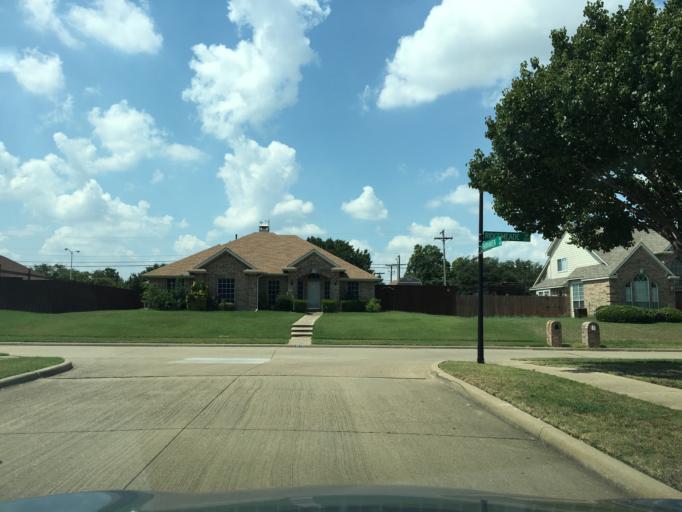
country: US
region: Texas
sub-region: Dallas County
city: Garland
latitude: 32.9409
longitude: -96.6471
